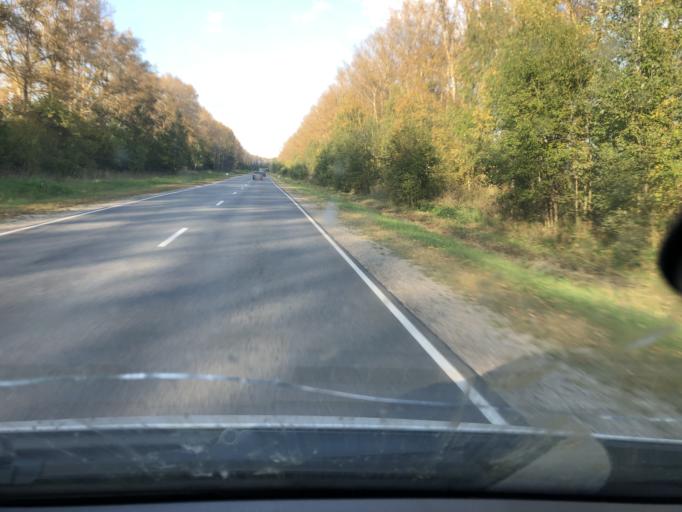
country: RU
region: Kaluga
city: Peremyshl'
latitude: 54.2368
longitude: 36.0680
